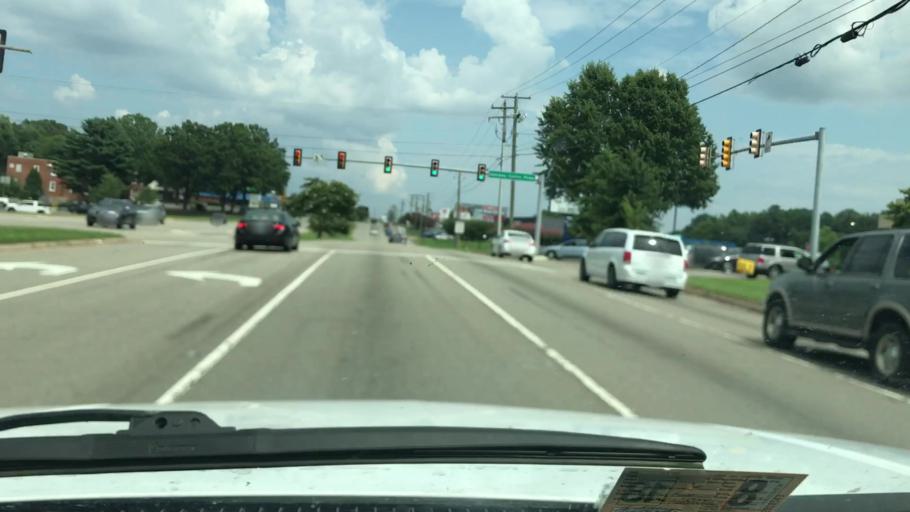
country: US
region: Virginia
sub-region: Chesterfield County
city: Bon Air
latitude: 37.4954
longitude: -77.5541
